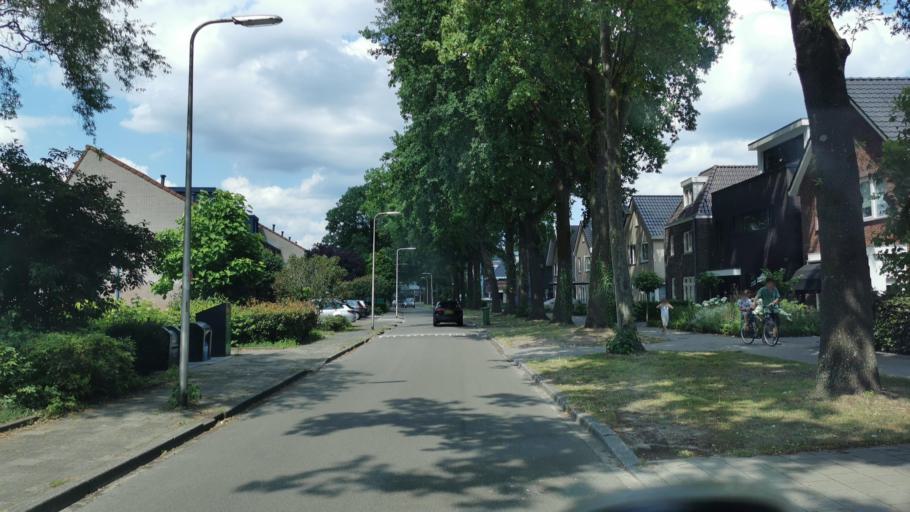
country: NL
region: Overijssel
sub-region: Gemeente Enschede
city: Enschede
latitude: 52.2353
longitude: 6.8953
